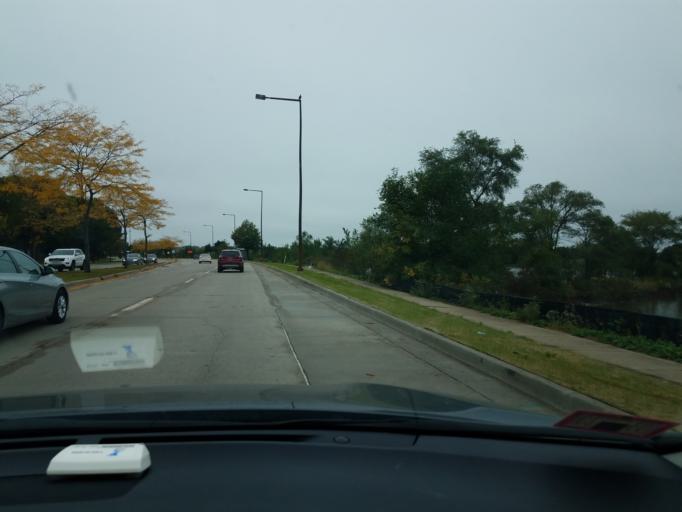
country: US
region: Illinois
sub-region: Lake County
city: Lincolnshire
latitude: 42.1684
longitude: -87.9277
